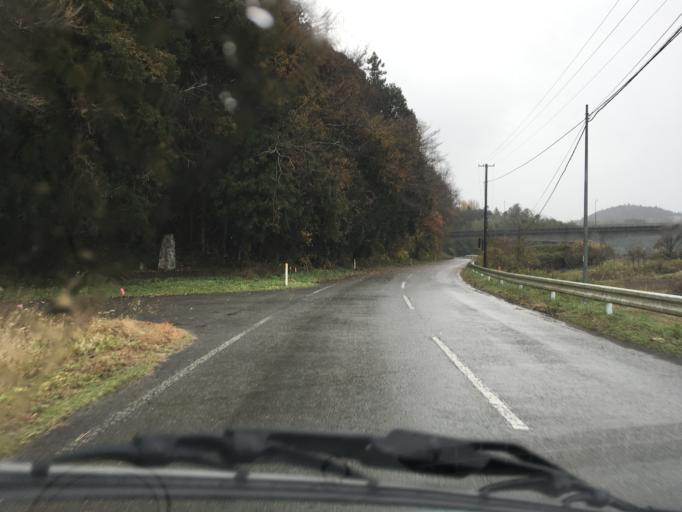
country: JP
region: Iwate
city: Ichinoseki
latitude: 38.7967
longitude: 141.2491
